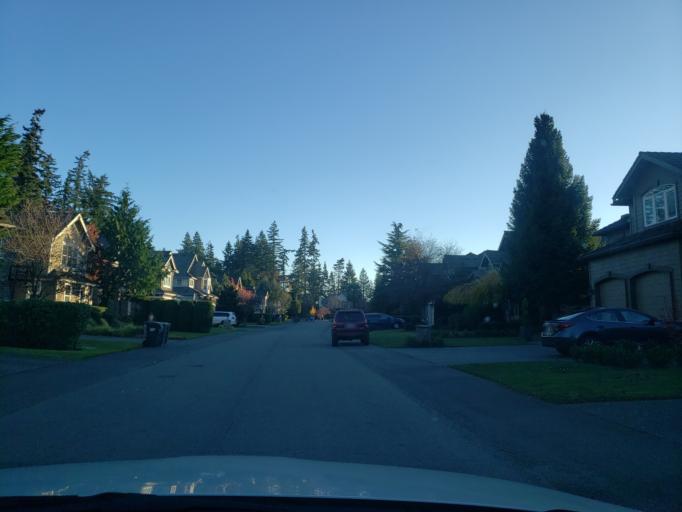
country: US
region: Washington
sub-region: Snohomish County
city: Woodway
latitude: 47.7799
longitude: -122.3782
